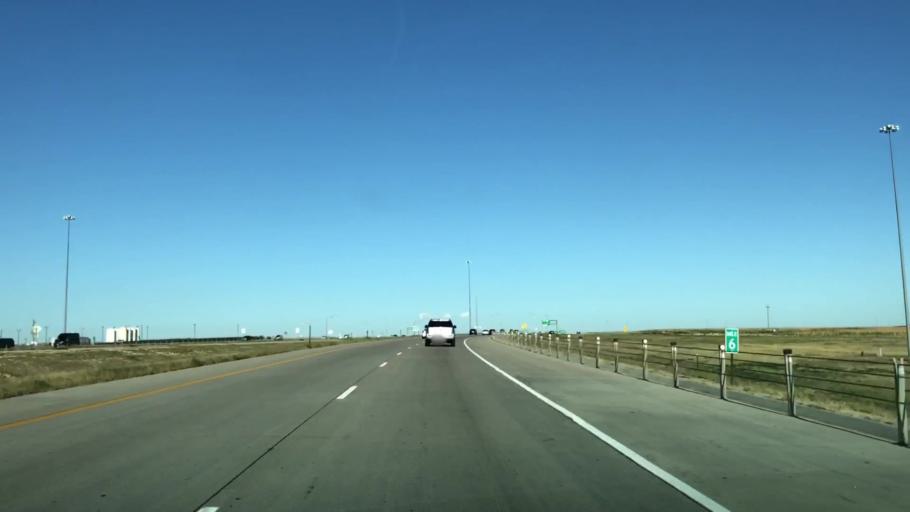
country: US
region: Colorado
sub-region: Adams County
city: Aurora
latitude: 39.8340
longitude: -104.7700
